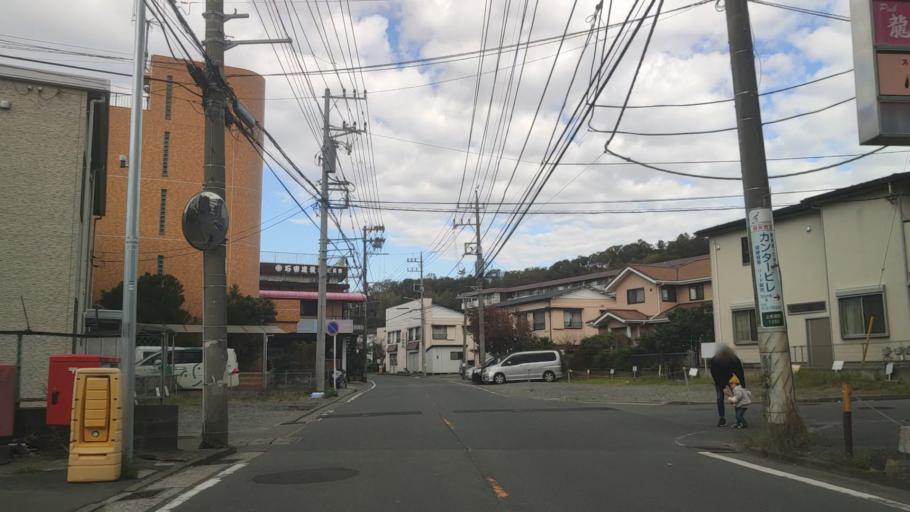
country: JP
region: Kanagawa
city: Minami-rinkan
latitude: 35.4252
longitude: 139.5295
